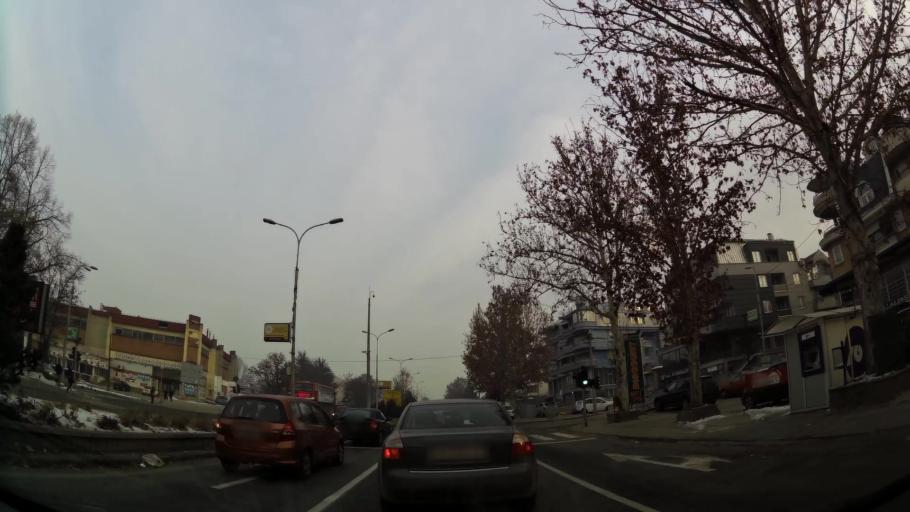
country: MK
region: Cair
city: Cair
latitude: 42.0210
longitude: 21.4490
